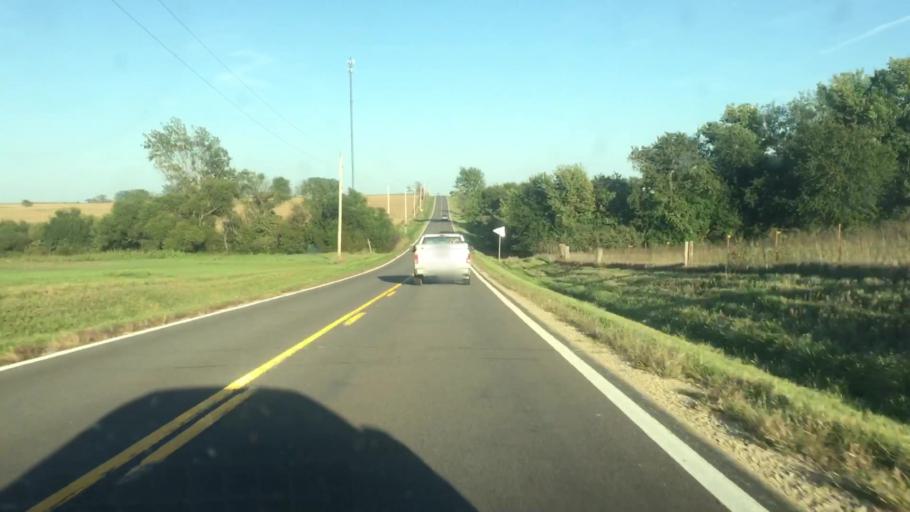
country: US
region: Kansas
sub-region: Brown County
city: Horton
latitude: 39.5513
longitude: -95.4313
